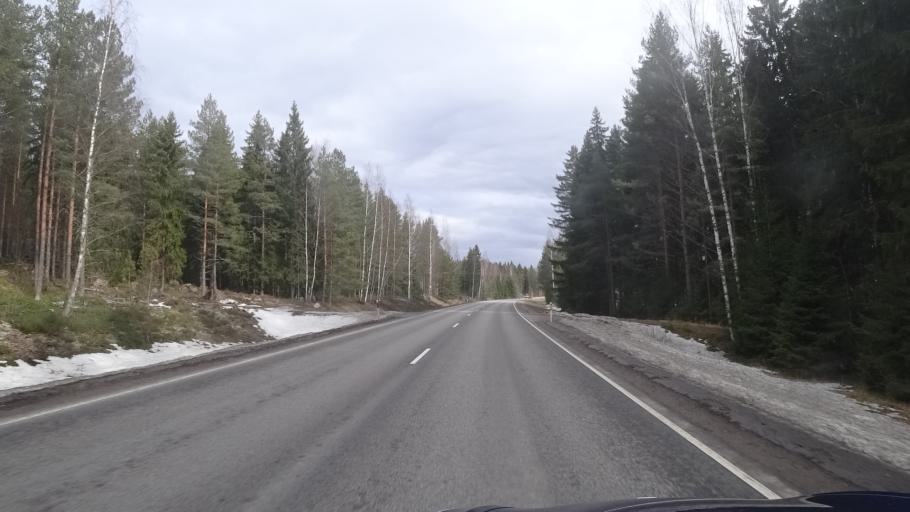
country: FI
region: Kymenlaakso
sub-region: Kouvola
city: Anjala
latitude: 60.6927
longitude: 26.7254
